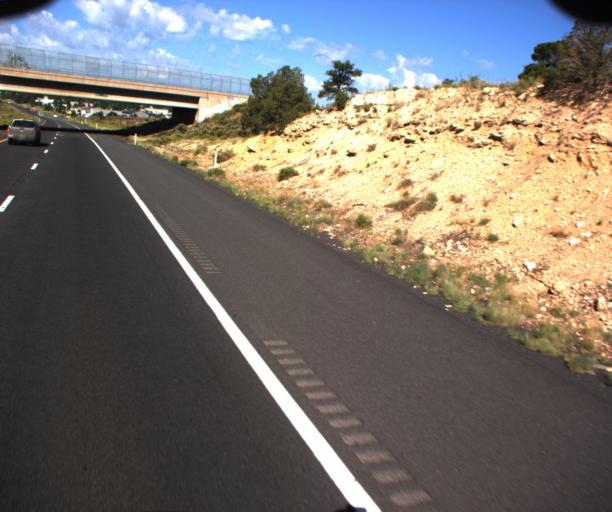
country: US
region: Arizona
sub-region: Coconino County
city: Flagstaff
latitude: 35.2171
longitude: -111.5819
